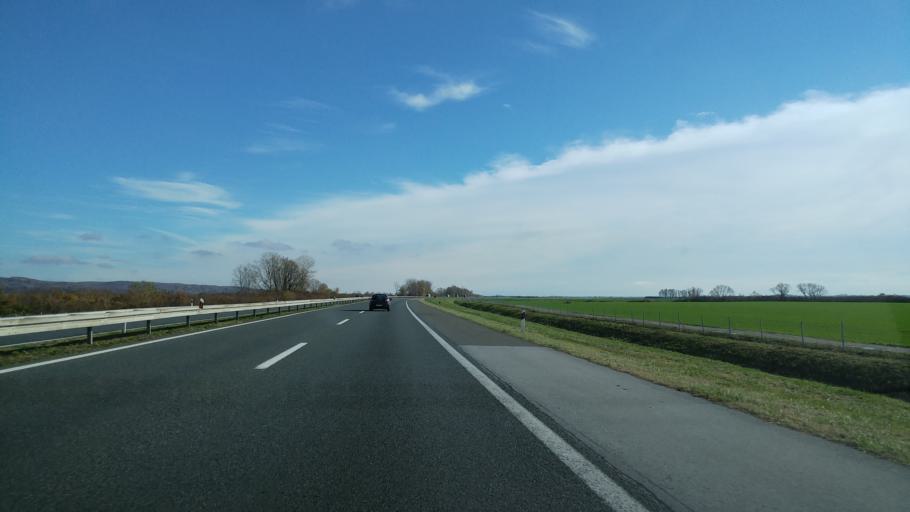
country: HR
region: Brodsko-Posavska
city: Okucani
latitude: 45.2888
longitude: 17.0978
